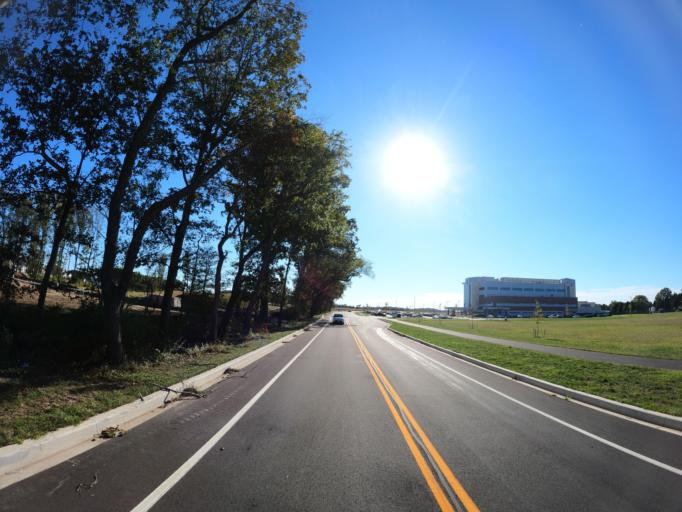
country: US
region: Delaware
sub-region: Sussex County
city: Lewes
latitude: 38.7234
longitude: -75.1375
